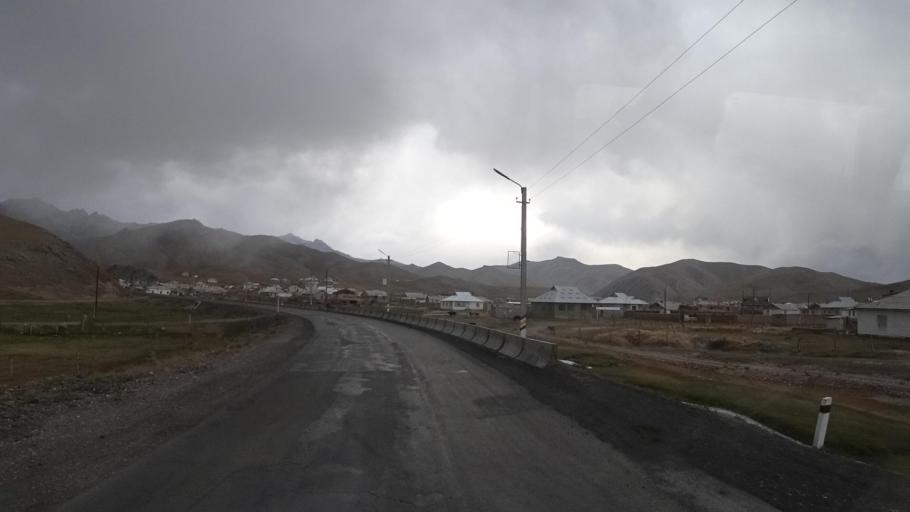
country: KG
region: Osh
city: Gul'cha
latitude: 39.7228
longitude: 73.2481
